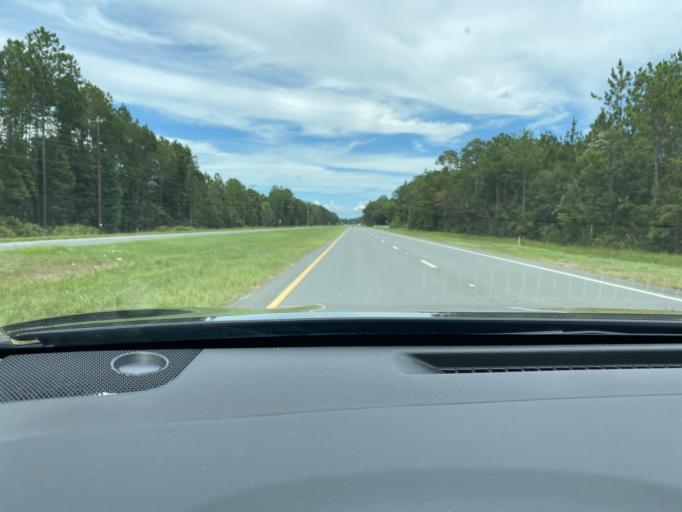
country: US
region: Georgia
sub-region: Brantley County
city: Nahunta
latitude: 31.1993
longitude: -82.0135
